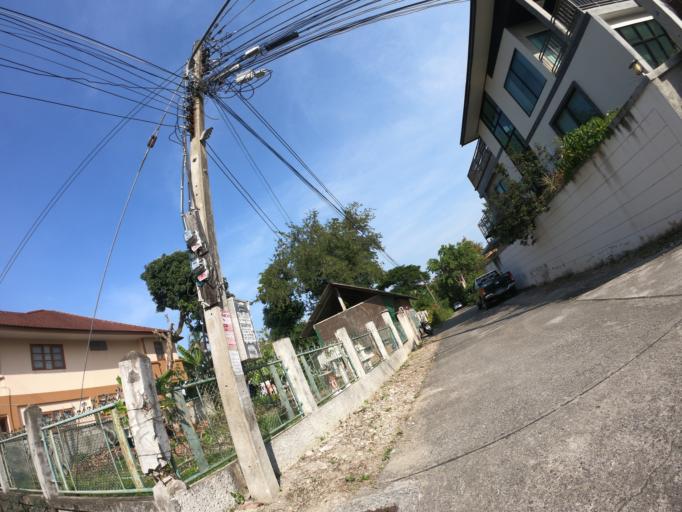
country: TH
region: Chiang Mai
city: Chiang Mai
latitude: 18.8176
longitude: 98.9866
